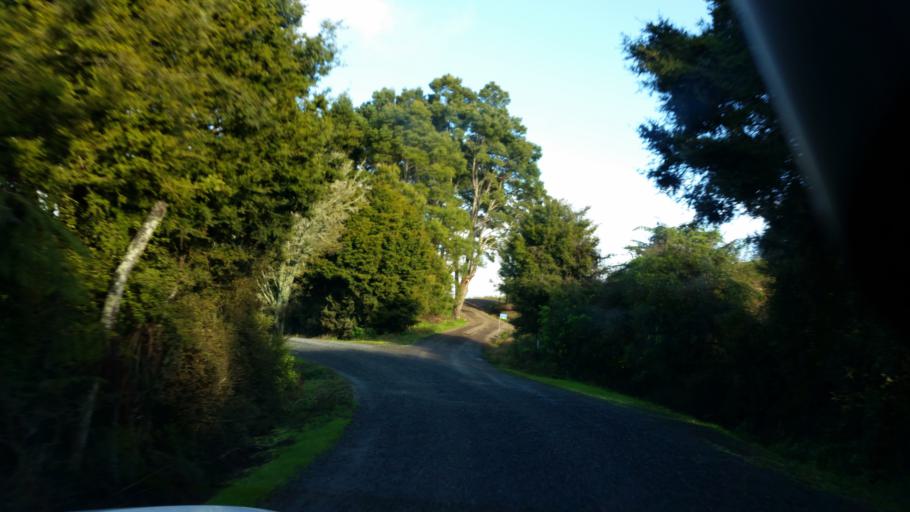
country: NZ
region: Northland
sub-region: Whangarei
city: Maungatapere
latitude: -35.6925
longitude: 174.1157
